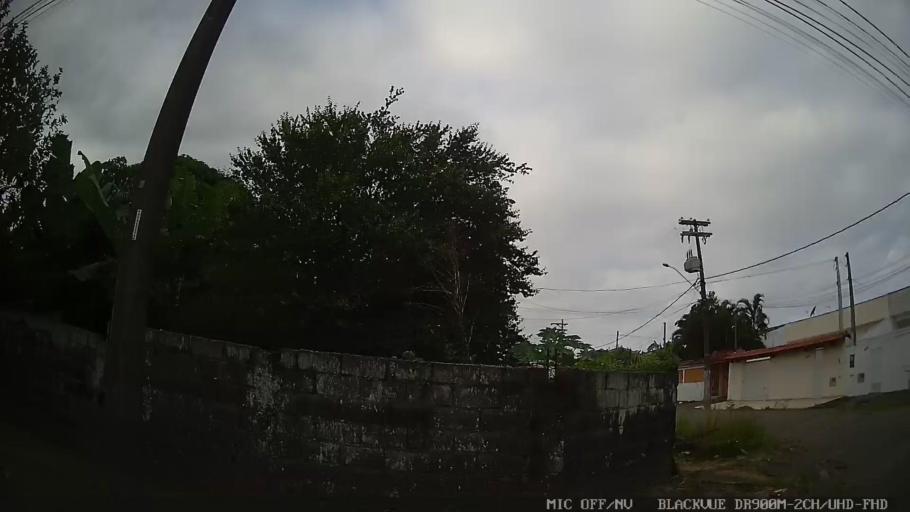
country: BR
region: Sao Paulo
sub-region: Peruibe
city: Peruibe
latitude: -24.3107
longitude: -46.9940
